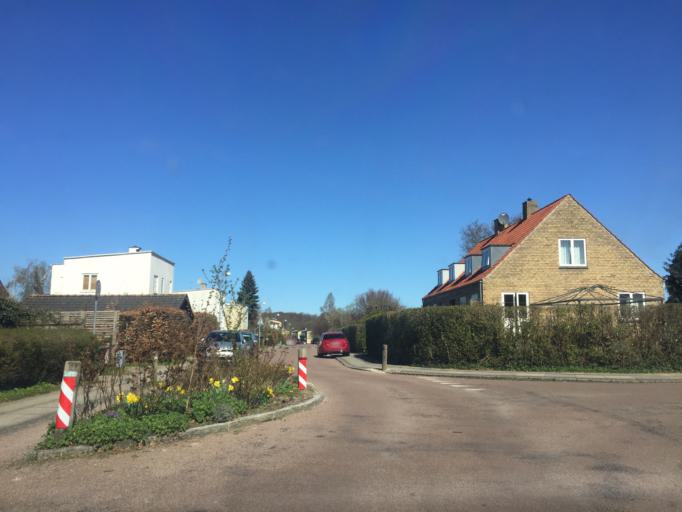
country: DK
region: Capital Region
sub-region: Rudersdal Kommune
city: Holte
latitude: 55.7932
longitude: 12.4807
